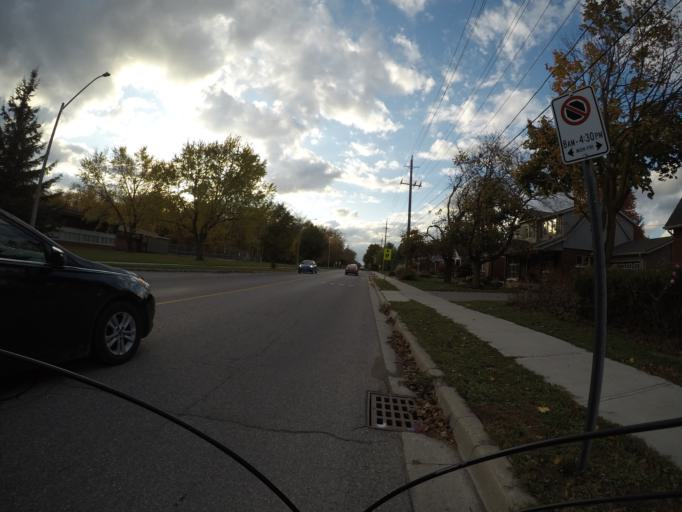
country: CA
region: Ontario
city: Waterloo
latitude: 43.5924
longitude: -80.5629
